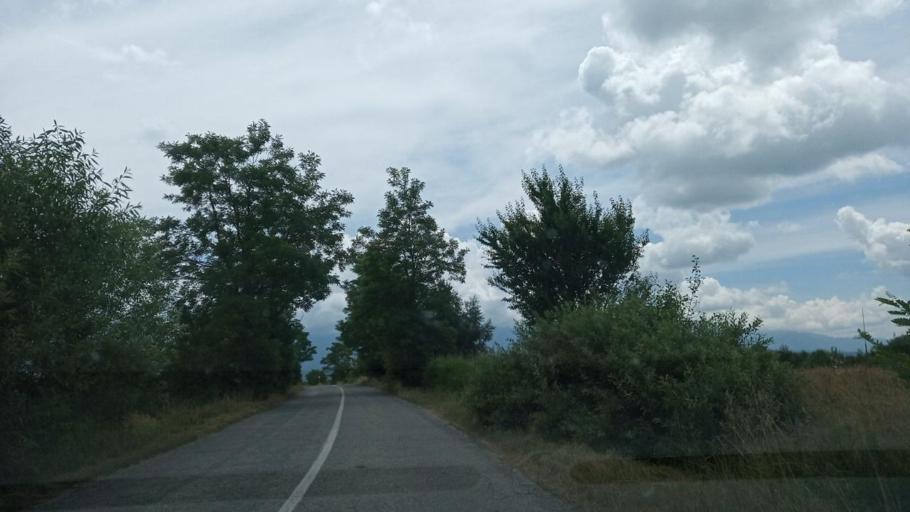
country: RO
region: Sibiu
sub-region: Comuna Porumbacu de Jos
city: Porumbacu de Jos
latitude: 45.7461
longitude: 24.4632
